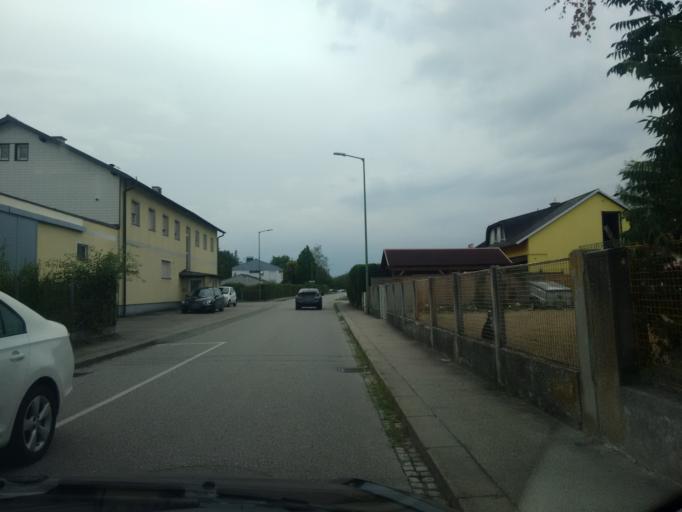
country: AT
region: Upper Austria
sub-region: Wels Stadt
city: Wels
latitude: 48.1823
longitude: 14.0681
